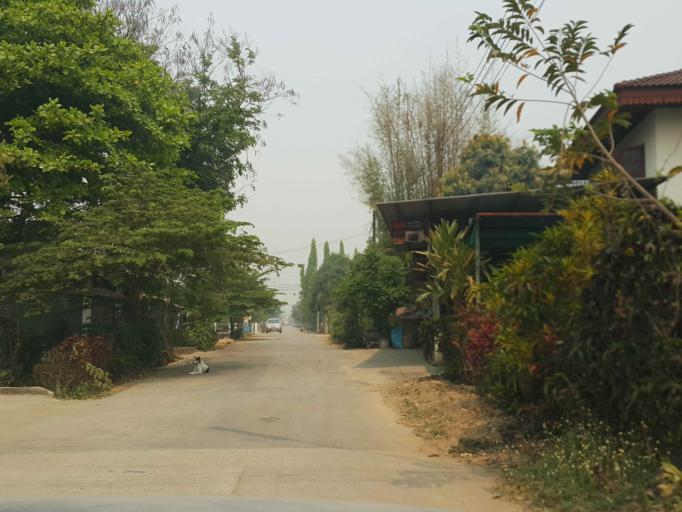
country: TH
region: Chiang Mai
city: Mae Taeng
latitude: 19.0783
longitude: 98.9380
